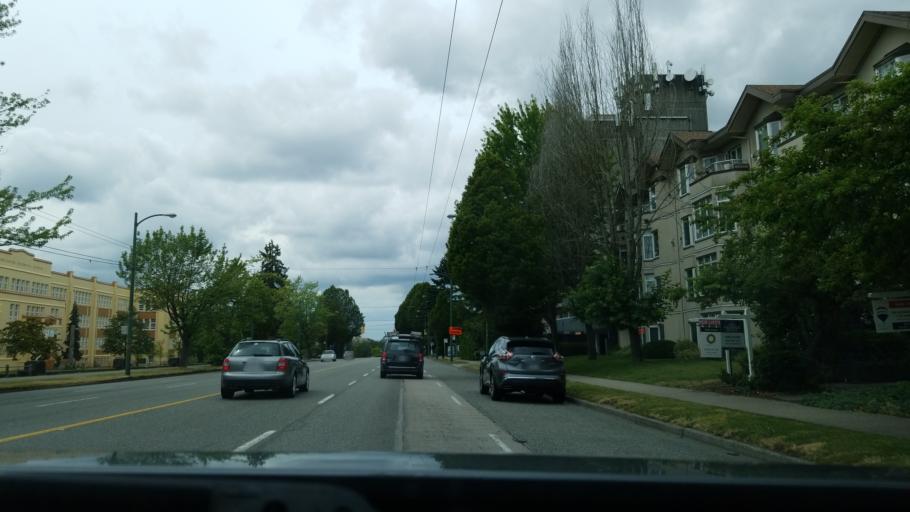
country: CA
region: British Columbia
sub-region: Fraser Valley Regional District
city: North Vancouver
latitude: 49.2620
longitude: -123.0501
